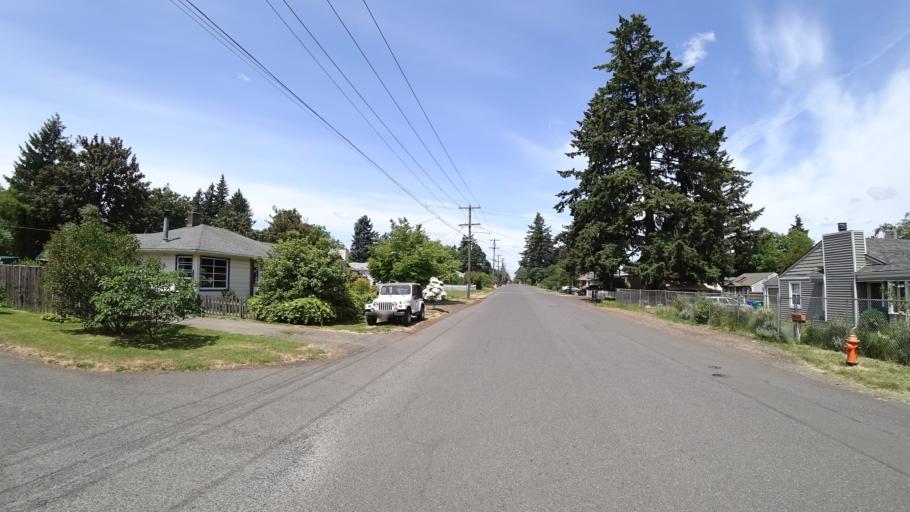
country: US
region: Oregon
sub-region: Multnomah County
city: Lents
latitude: 45.4645
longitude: -122.6023
